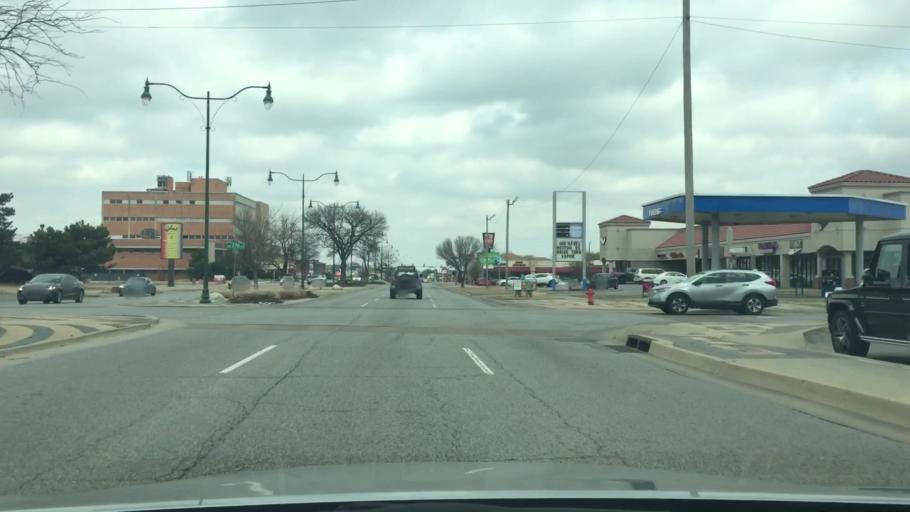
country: US
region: Oklahoma
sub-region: Oklahoma County
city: Oklahoma City
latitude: 35.4972
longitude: -97.5342
